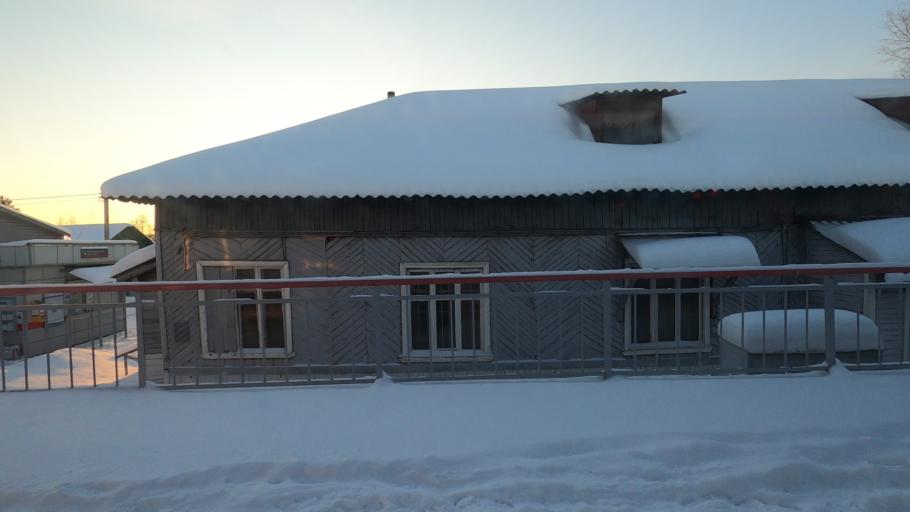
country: RU
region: Moskovskaya
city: Dmitrov
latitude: 56.3837
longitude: 37.5151
